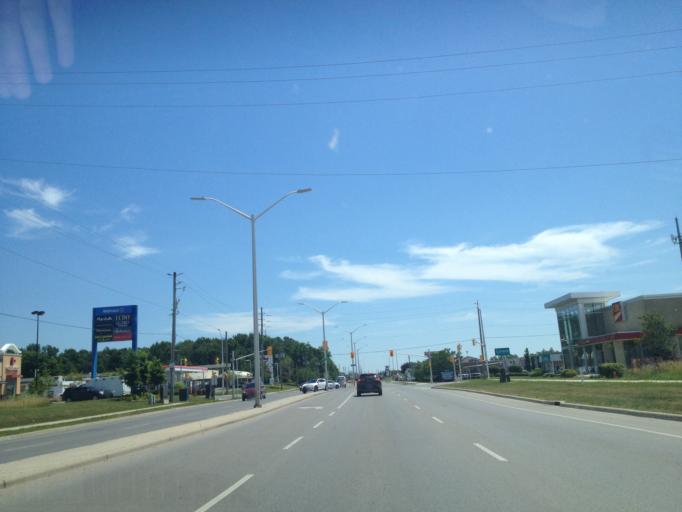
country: CA
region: Ontario
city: London
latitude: 43.0091
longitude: -81.3374
